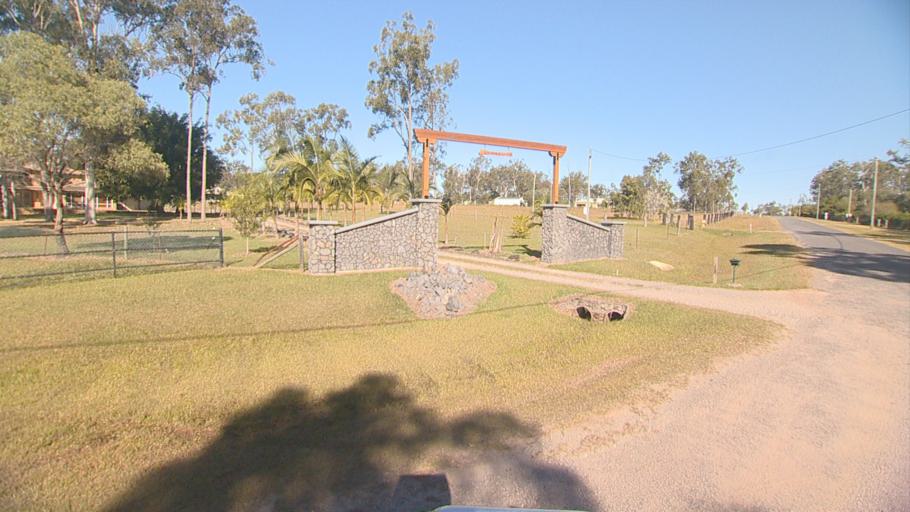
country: AU
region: Queensland
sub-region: Logan
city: Logan Reserve
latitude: -27.7254
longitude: 153.0674
